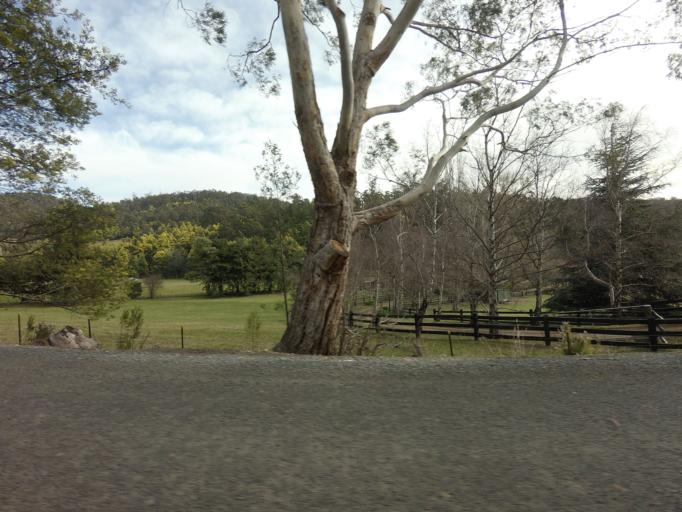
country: AU
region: Tasmania
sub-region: Kingborough
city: Margate
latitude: -42.9906
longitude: 147.1880
